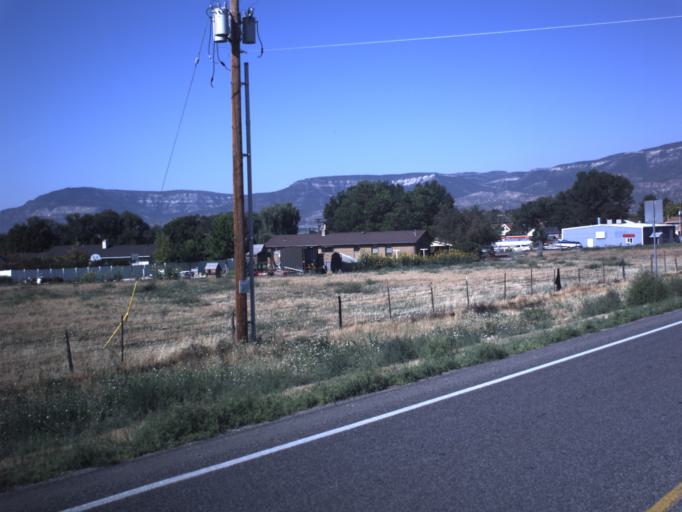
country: US
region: Utah
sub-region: Sanpete County
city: Moroni
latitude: 39.5249
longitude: -111.5744
